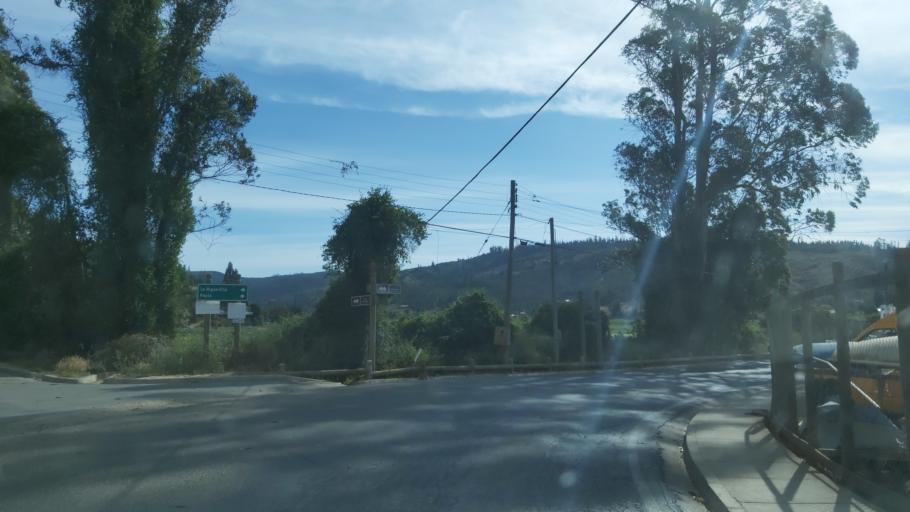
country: CL
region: Maule
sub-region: Provincia de Talca
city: Constitucion
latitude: -34.8517
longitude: -72.0393
